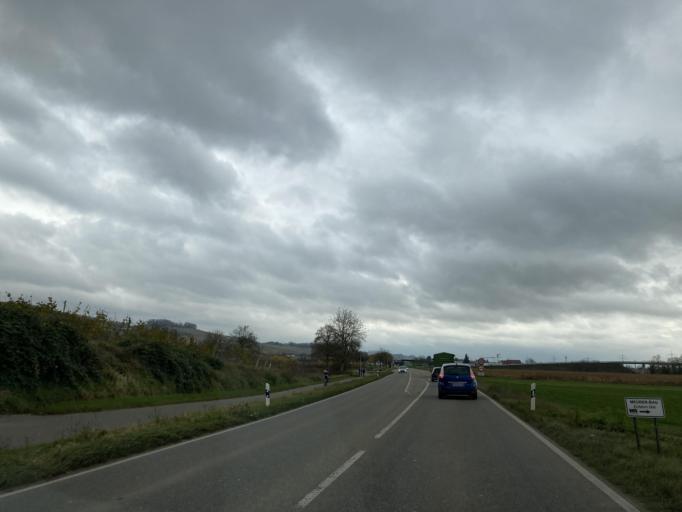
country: DE
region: Baden-Wuerttemberg
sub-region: Freiburg Region
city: Auggen
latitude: 47.8009
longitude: 7.5973
